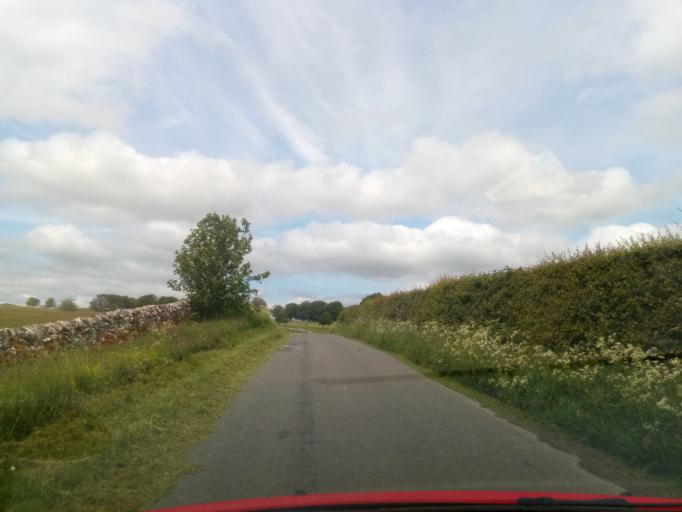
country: GB
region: Scotland
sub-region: The Scottish Borders
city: Selkirk
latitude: 55.5131
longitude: -2.8105
